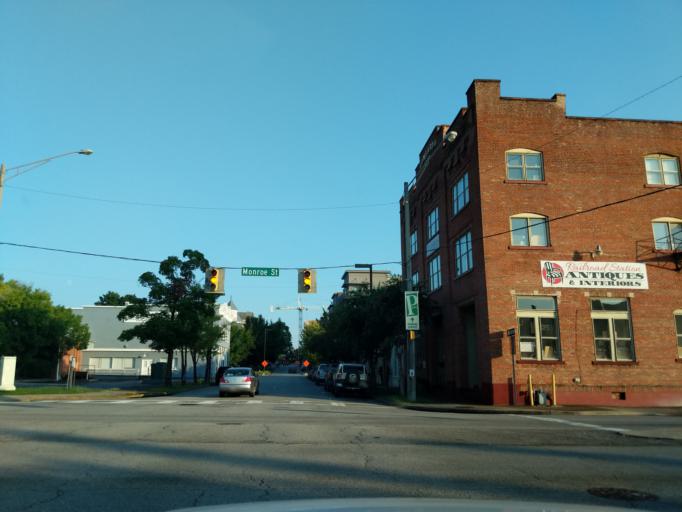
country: US
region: Alabama
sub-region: Madison County
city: Huntsville
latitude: 34.7340
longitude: -86.5887
